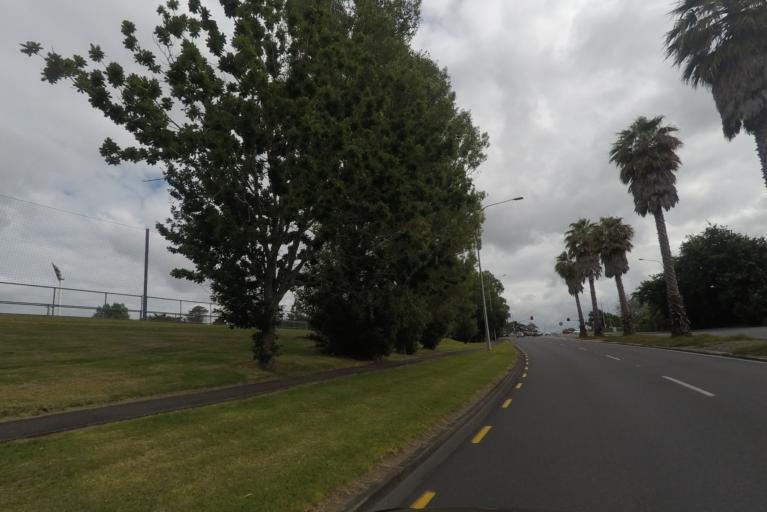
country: NZ
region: Auckland
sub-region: Auckland
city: Rothesay Bay
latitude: -36.7257
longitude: 174.6988
